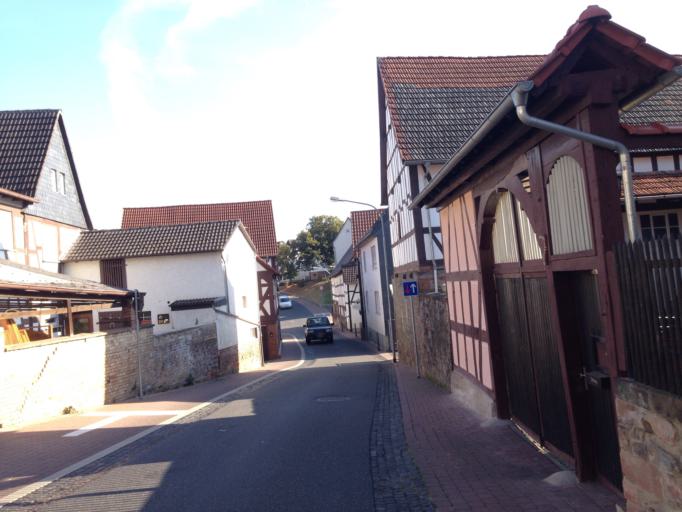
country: DE
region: Hesse
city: Lollar
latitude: 50.6356
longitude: 8.6762
